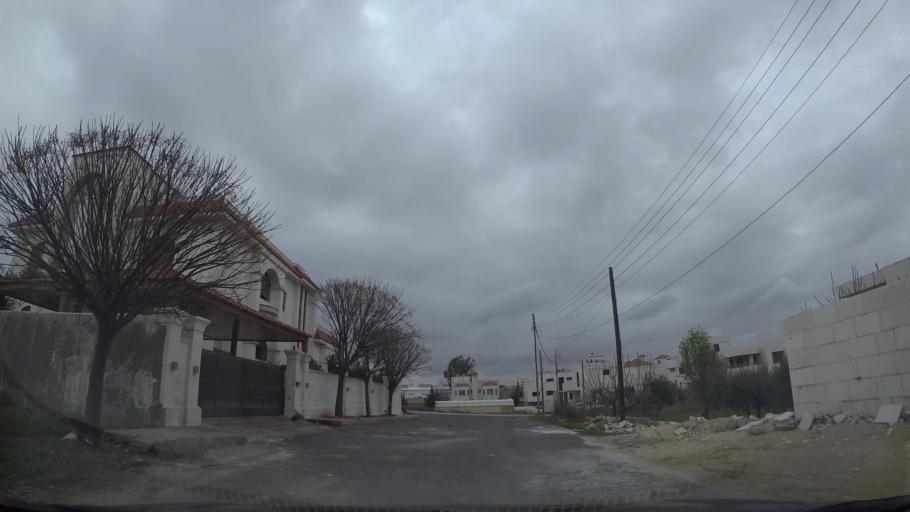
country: JO
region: Amman
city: Umm as Summaq
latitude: 31.9256
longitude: 35.8573
